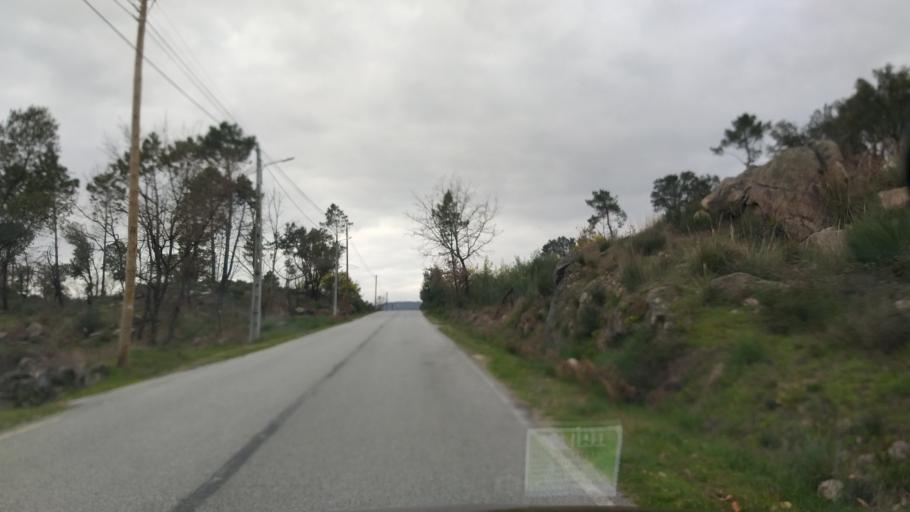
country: PT
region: Guarda
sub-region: Fornos de Algodres
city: Fornos de Algodres
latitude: 40.5745
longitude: -7.6062
